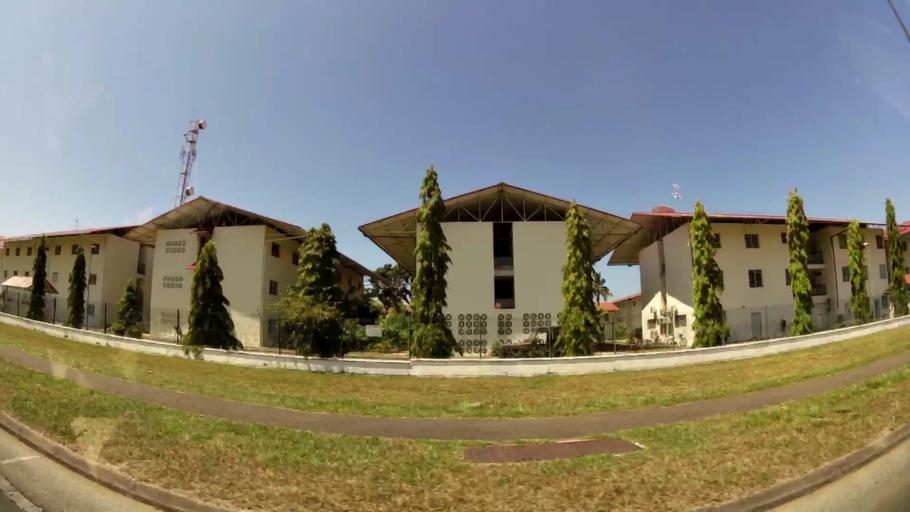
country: GF
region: Guyane
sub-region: Guyane
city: Kourou
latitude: 5.1689
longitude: -52.6462
